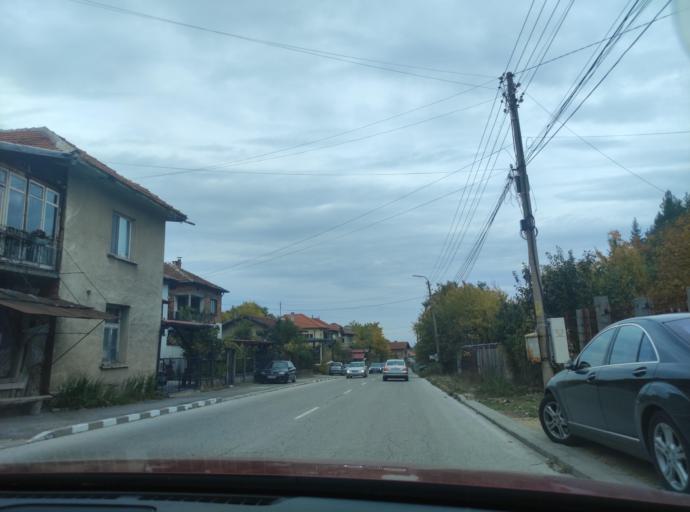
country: BG
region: Montana
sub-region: Obshtina Berkovitsa
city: Berkovitsa
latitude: 43.1924
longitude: 23.1600
